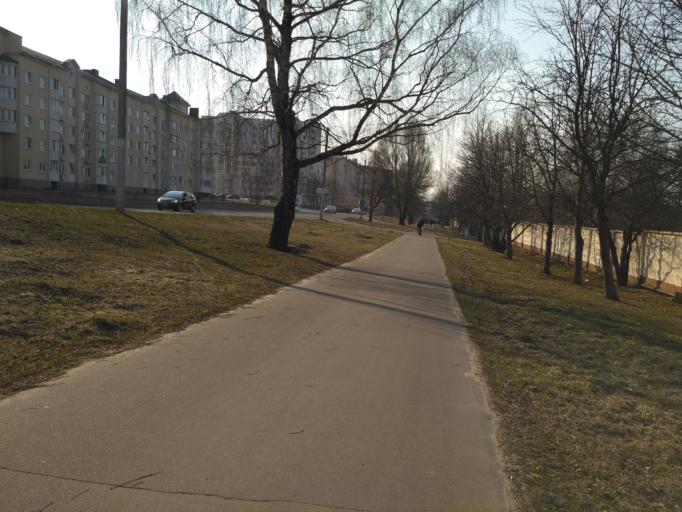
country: BY
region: Minsk
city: Zaslawye
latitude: 54.0127
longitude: 27.2639
